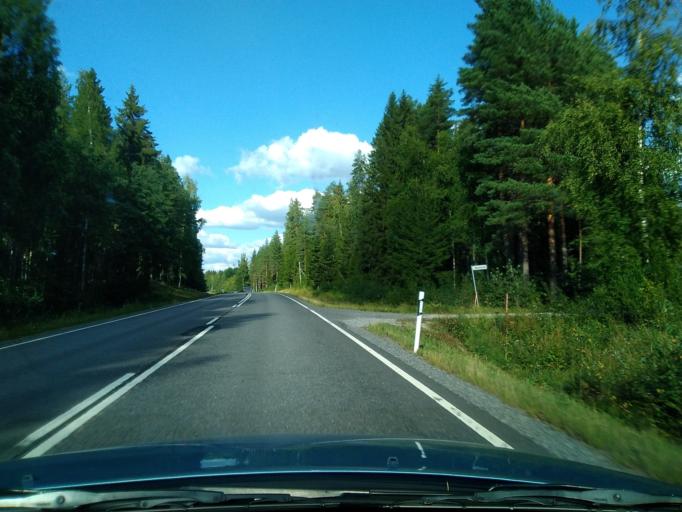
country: FI
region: Pirkanmaa
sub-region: Ylae-Pirkanmaa
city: Maenttae
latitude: 61.9848
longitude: 24.6272
